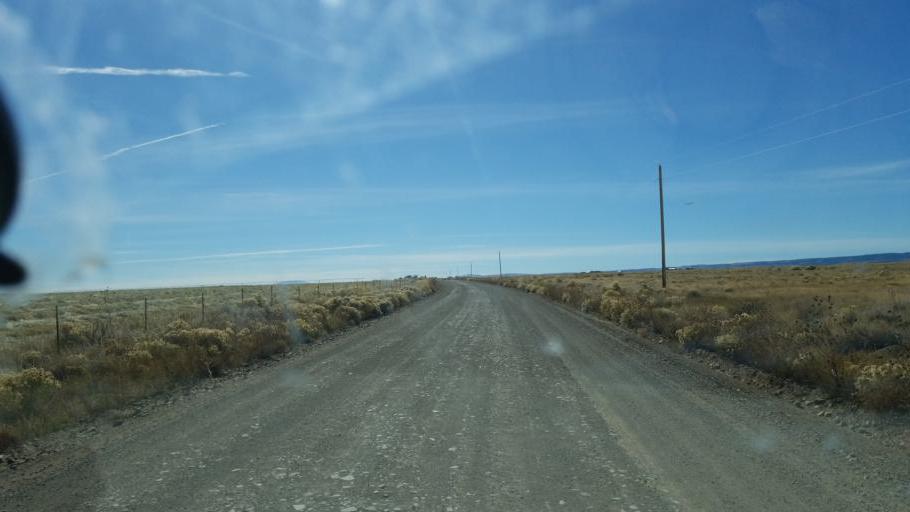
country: US
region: Colorado
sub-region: Rio Grande County
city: Monte Vista
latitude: 37.3970
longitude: -106.1494
